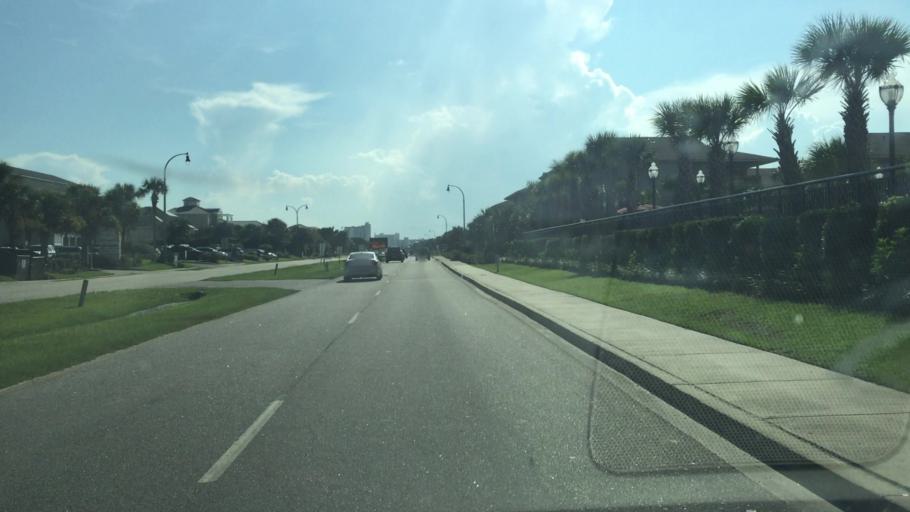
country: US
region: South Carolina
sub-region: Horry County
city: North Myrtle Beach
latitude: 33.8223
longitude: -78.6675
